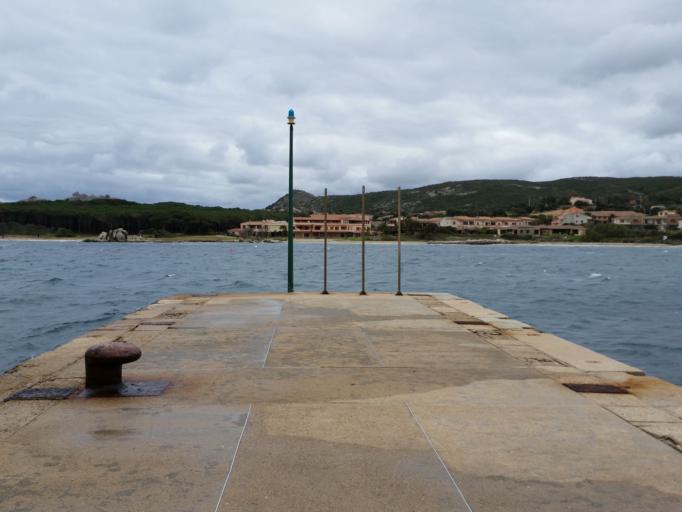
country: IT
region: Sardinia
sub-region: Provincia di Olbia-Tempio
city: Palau
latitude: 41.1808
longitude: 9.3869
